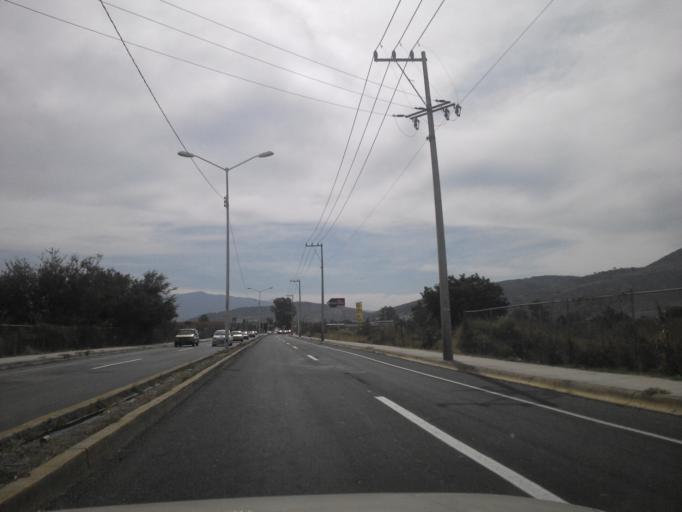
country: MX
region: Jalisco
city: San Sebastian el Grande
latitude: 20.5181
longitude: -103.4105
